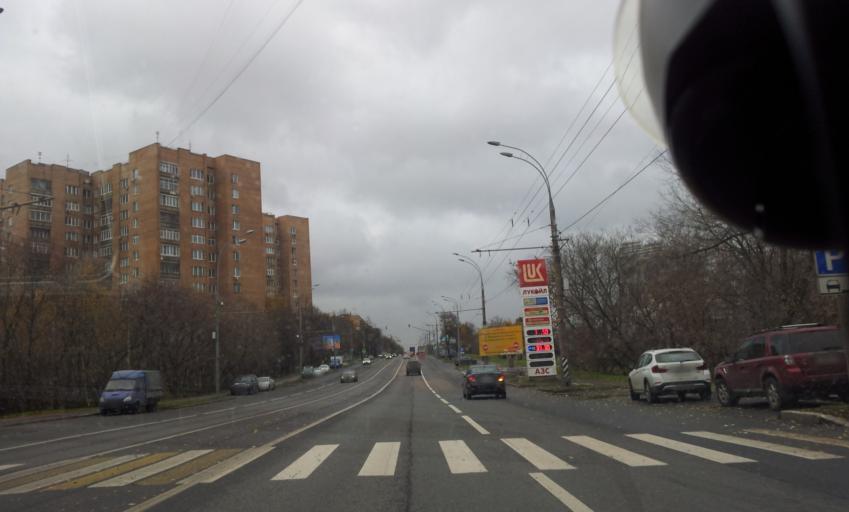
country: RU
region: Moscow
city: Vorob'yovo
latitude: 55.7194
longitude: 37.5224
